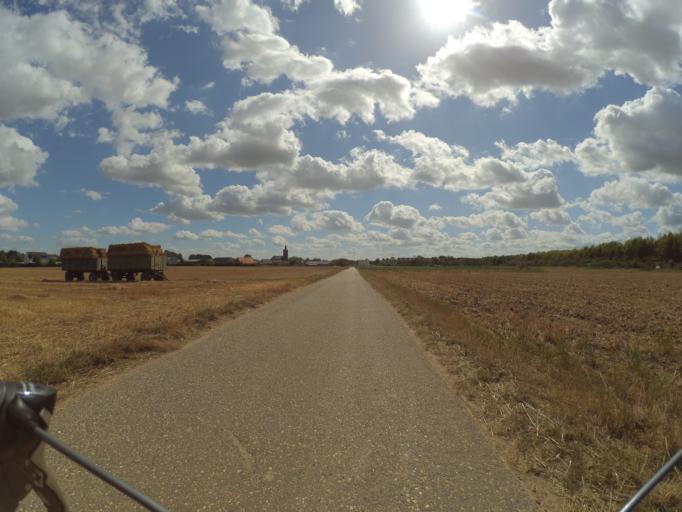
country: DE
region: North Rhine-Westphalia
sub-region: Regierungsbezirk Koln
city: Inden
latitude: 50.8787
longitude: 6.3911
